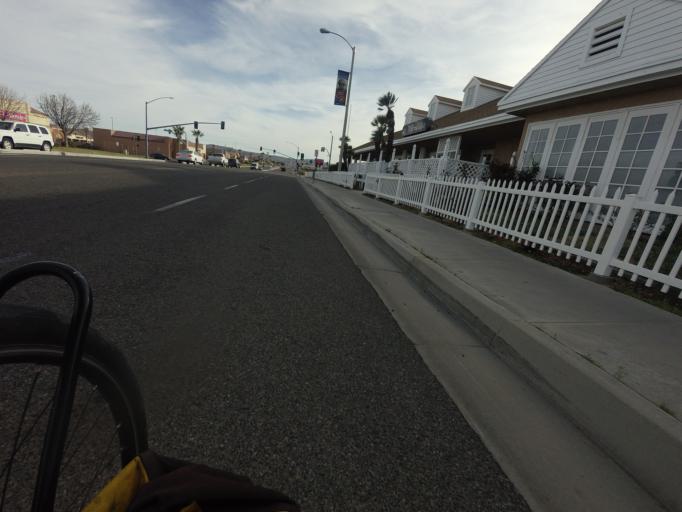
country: US
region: California
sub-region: Kern County
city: Ridgecrest
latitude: 35.6377
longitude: -117.6700
